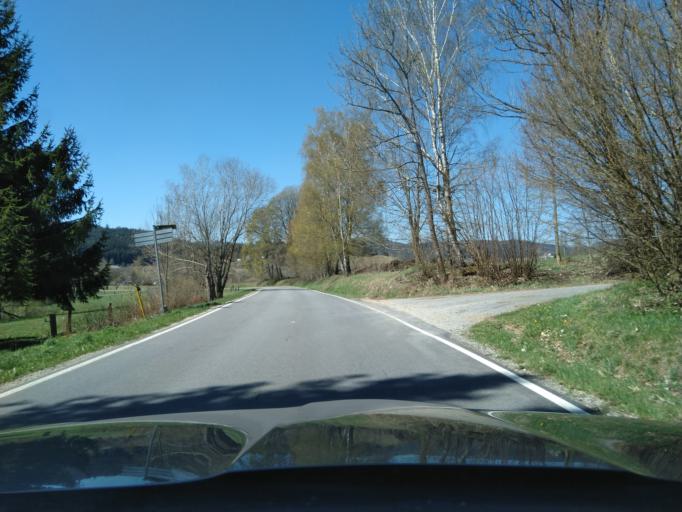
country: CZ
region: Jihocesky
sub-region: Okres Prachatice
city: Vimperk
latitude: 48.9558
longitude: 13.7693
